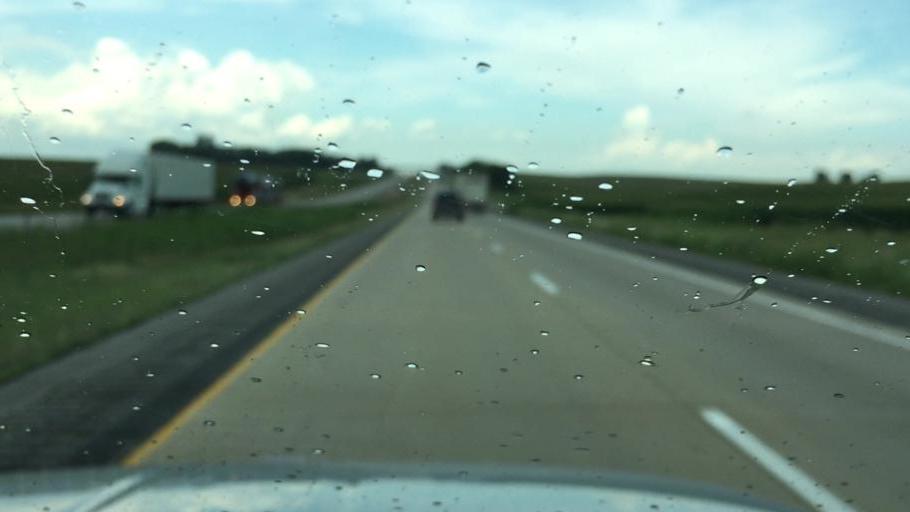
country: US
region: Iowa
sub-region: Poweshiek County
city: Brooklyn
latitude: 41.6960
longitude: -92.2526
